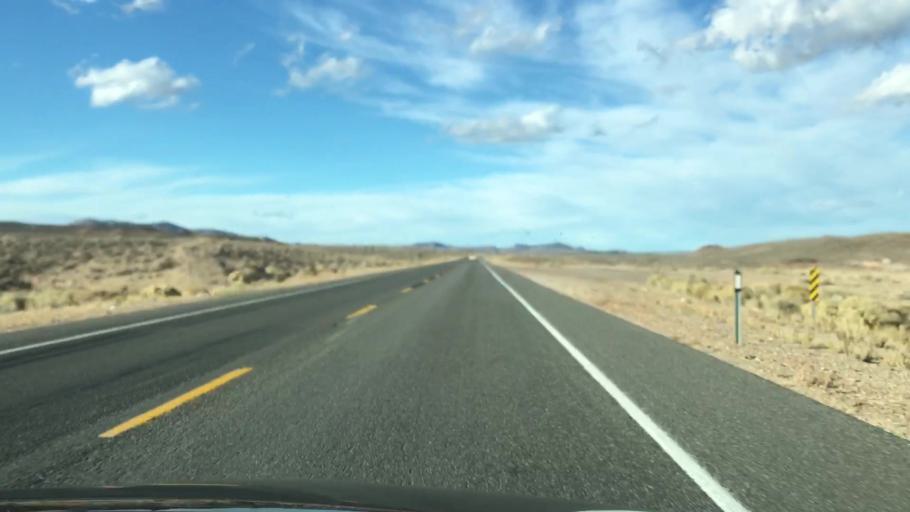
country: US
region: Nevada
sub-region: Esmeralda County
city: Goldfield
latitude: 37.5366
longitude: -117.1940
